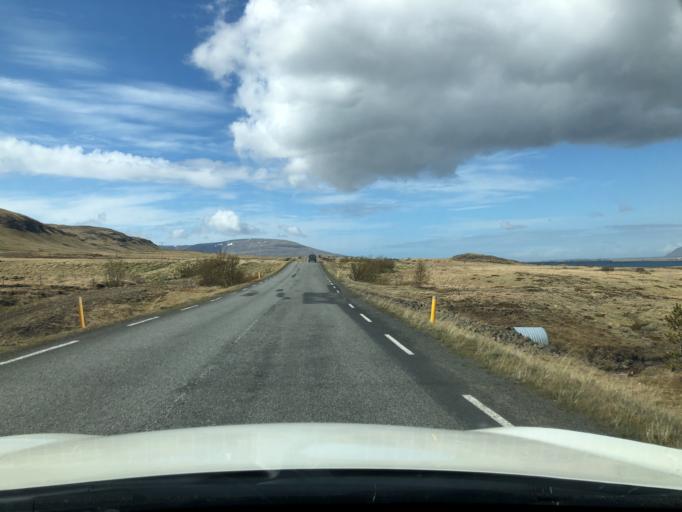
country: IS
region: Capital Region
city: Mosfellsbaer
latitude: 64.3300
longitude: -21.6706
